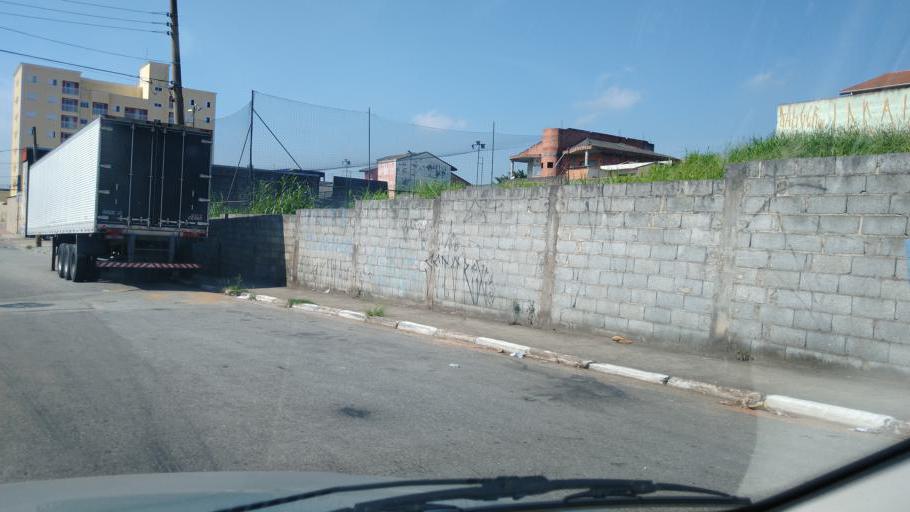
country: BR
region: Sao Paulo
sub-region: Aruja
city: Aruja
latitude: -23.4097
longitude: -46.4032
